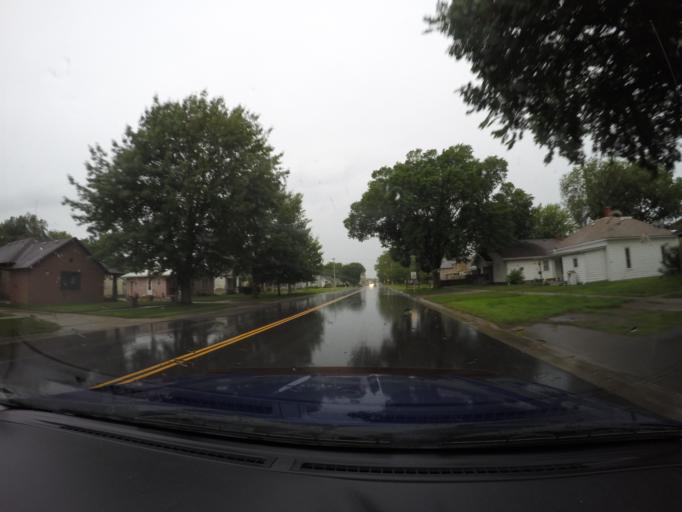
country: US
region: Kansas
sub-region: Cloud County
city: Concordia
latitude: 39.5716
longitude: -97.6529
